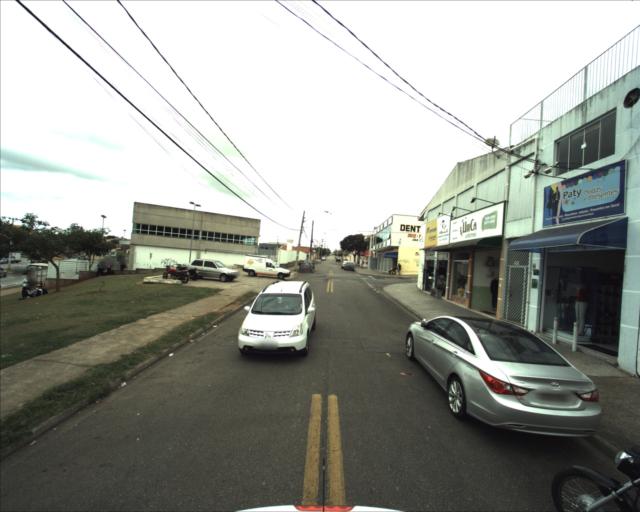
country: BR
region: Sao Paulo
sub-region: Sorocaba
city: Sorocaba
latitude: -23.5042
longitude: -47.5151
